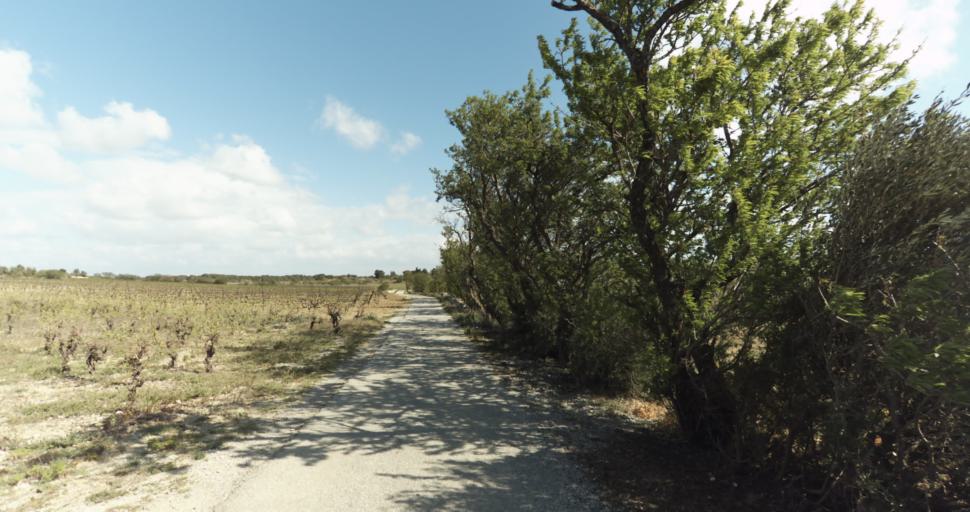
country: FR
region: Languedoc-Roussillon
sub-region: Departement de l'Aude
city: Leucate
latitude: 42.9220
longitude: 3.0365
